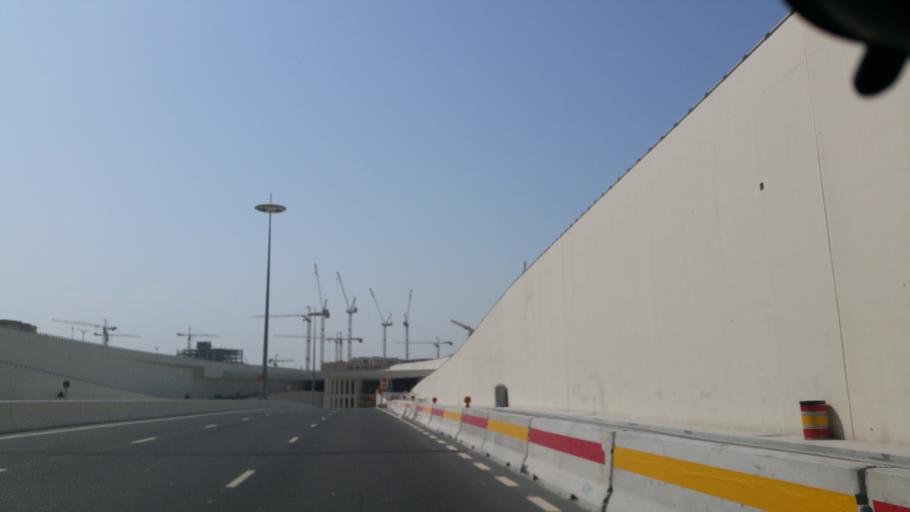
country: QA
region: Baladiyat Umm Salal
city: Umm Salal Muhammad
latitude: 25.4122
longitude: 51.5092
